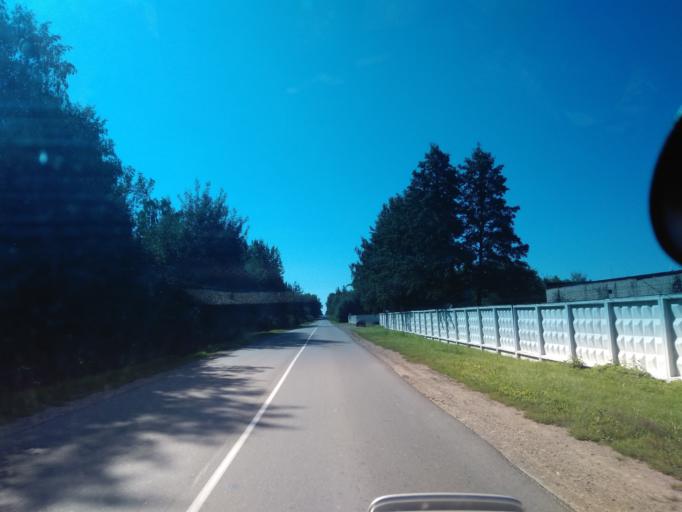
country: BY
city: Fanipol
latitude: 53.7095
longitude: 27.3474
